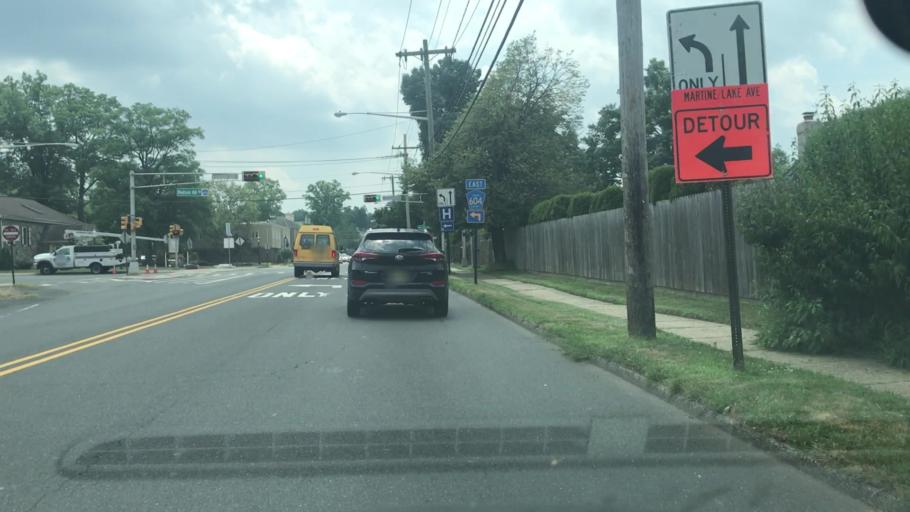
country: US
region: New Jersey
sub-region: Union County
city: Clark
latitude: 40.6196
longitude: -74.3222
